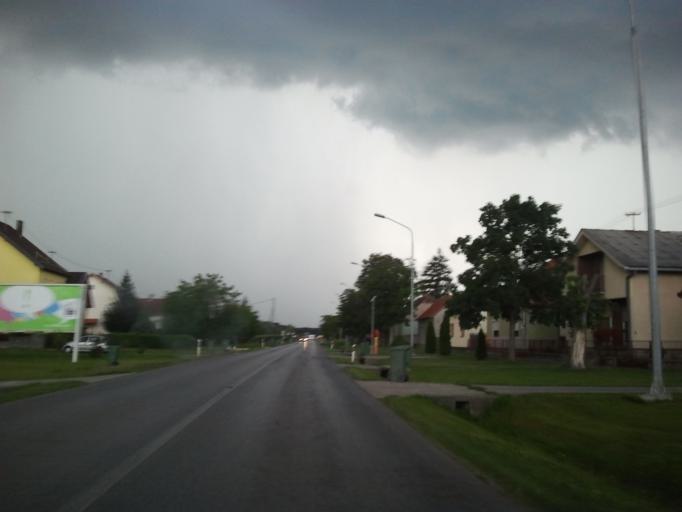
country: HR
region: Osjecko-Baranjska
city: Ladimirevci
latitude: 45.6412
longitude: 18.4621
